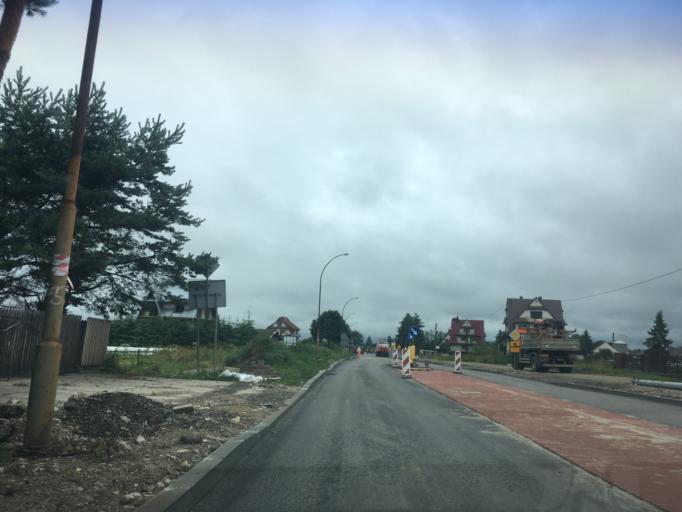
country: PL
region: Lesser Poland Voivodeship
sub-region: Powiat nowotarski
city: Czarny Dunajec
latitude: 49.4437
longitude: 19.8545
